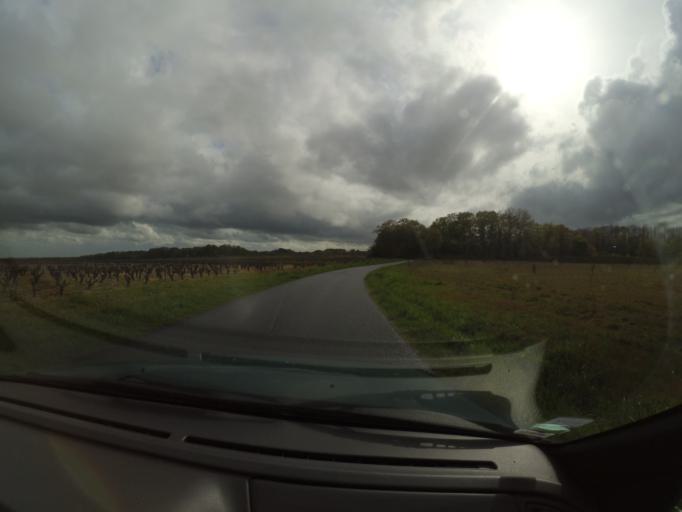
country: FR
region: Pays de la Loire
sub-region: Departement de la Loire-Atlantique
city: Monnieres
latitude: 47.1200
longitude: -1.3575
